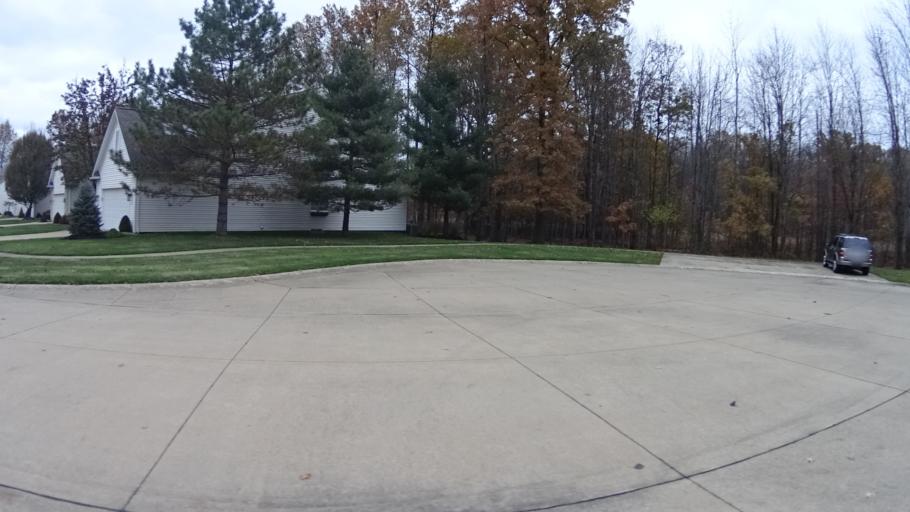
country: US
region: Ohio
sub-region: Lorain County
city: Avon Center
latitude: 41.4852
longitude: -81.9759
